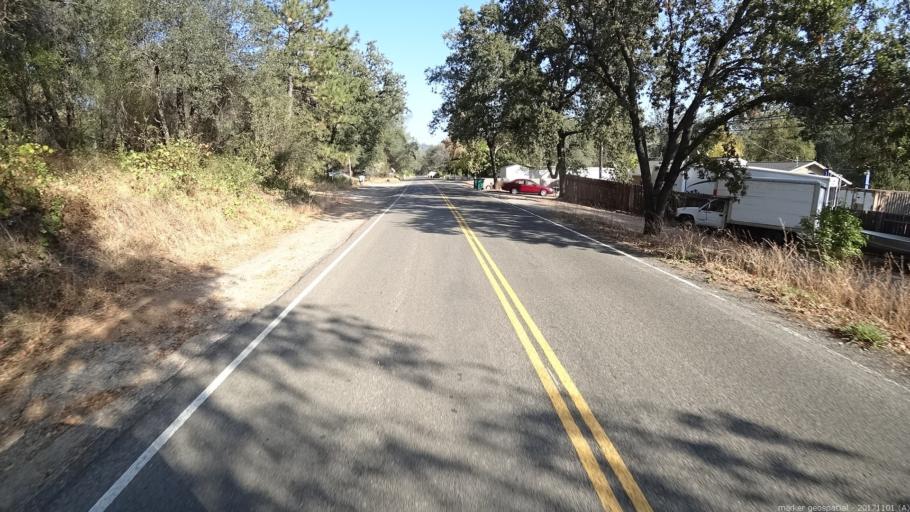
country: US
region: California
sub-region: Shasta County
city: Shasta Lake
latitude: 40.7255
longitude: -122.3252
